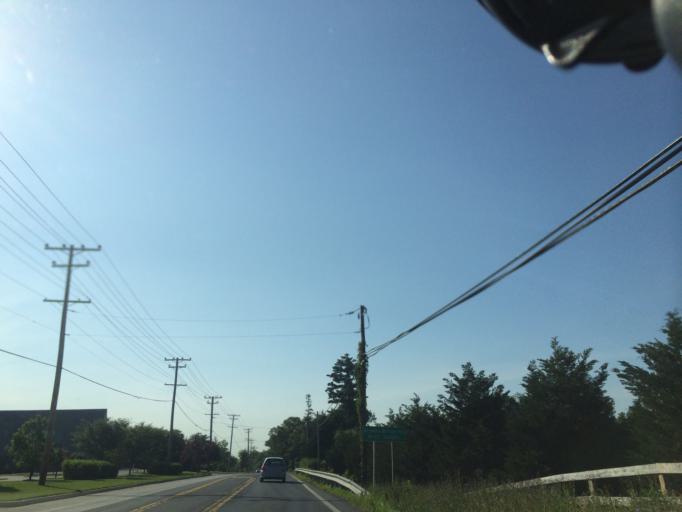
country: US
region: Maryland
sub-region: Howard County
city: Highland
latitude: 39.1682
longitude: -76.9465
